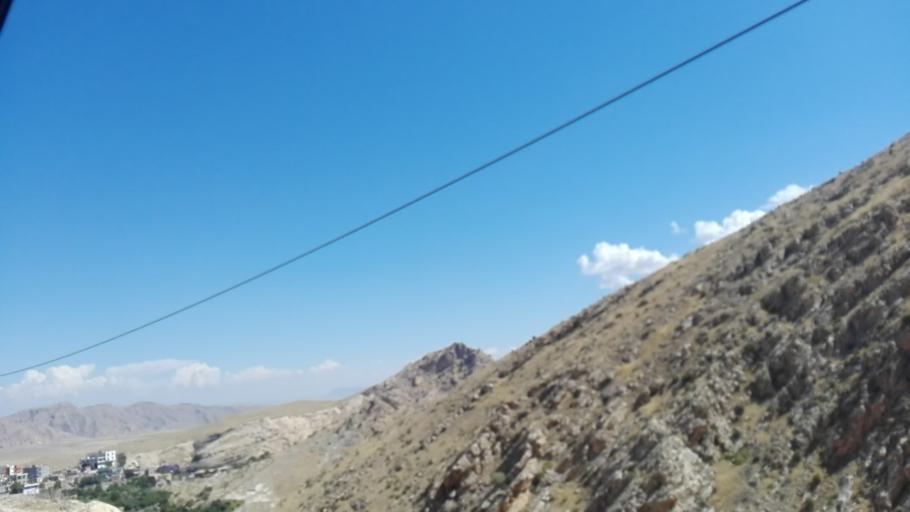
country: TR
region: Batman
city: Hasankeyf
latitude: 37.7015
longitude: 41.4612
